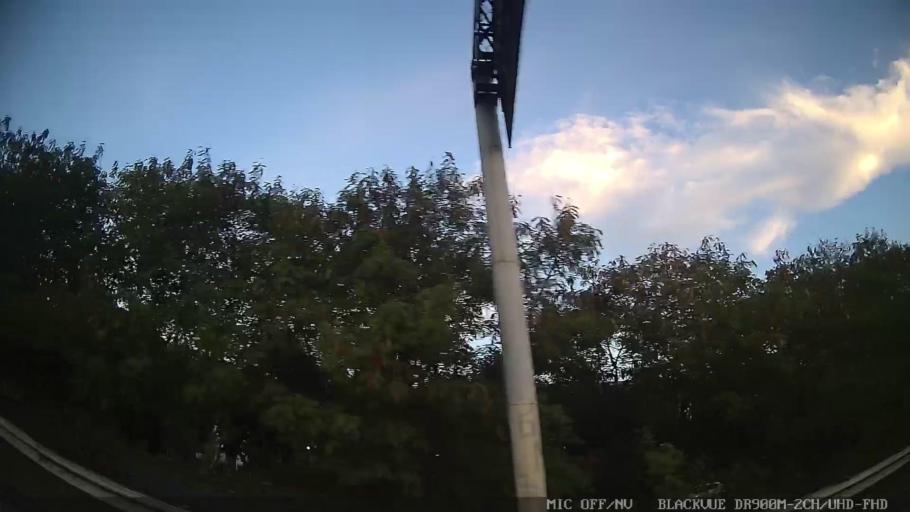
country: BR
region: Sao Paulo
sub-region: Indaiatuba
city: Indaiatuba
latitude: -23.1285
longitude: -47.2311
